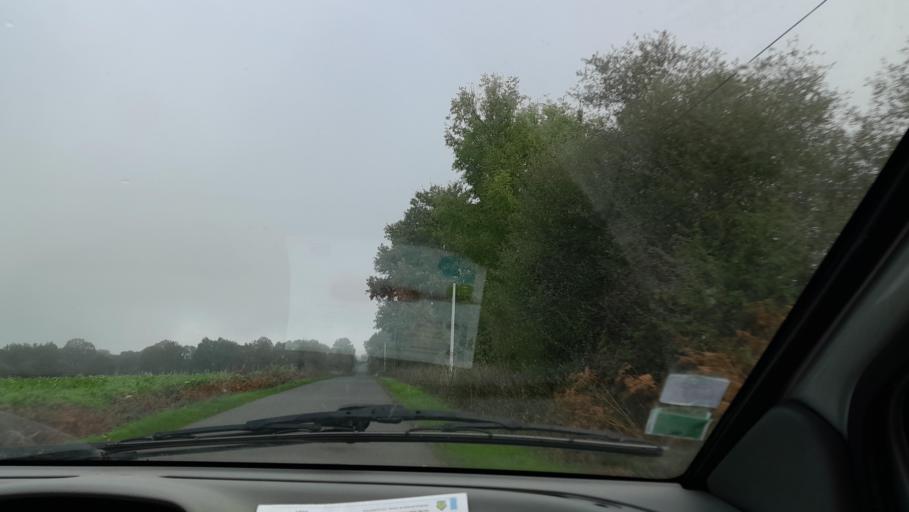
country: FR
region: Pays de la Loire
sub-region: Departement de la Mayenne
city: Saint-Pierre-la-Cour
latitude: 48.1522
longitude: -1.0322
